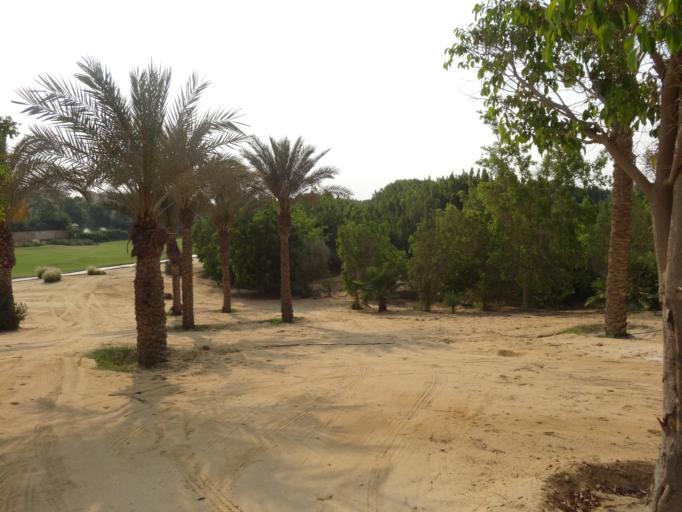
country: EG
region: Muhafazat al Qalyubiyah
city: Al Khankah
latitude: 30.0681
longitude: 31.4346
